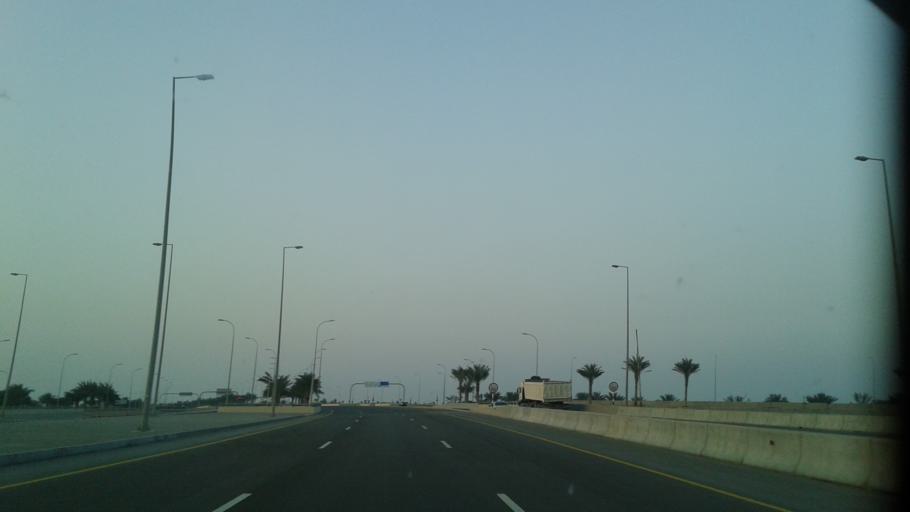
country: OM
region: Muhafazat Masqat
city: Bawshar
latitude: 23.5894
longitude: 58.3328
